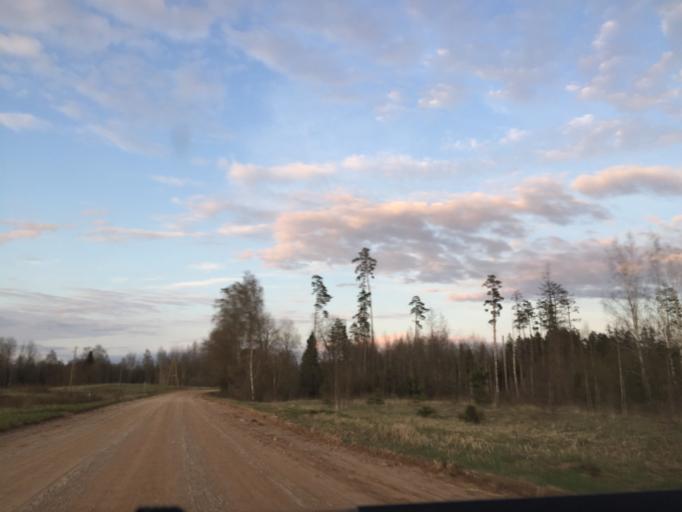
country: LV
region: Gulbenes Rajons
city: Gulbene
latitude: 57.2447
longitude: 26.8553
